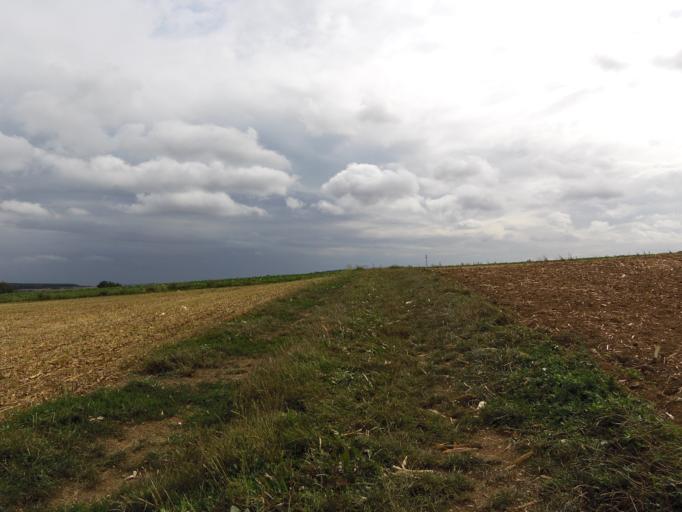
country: DE
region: Bavaria
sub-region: Regierungsbezirk Unterfranken
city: Rimpar
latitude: 49.8548
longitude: 9.9442
